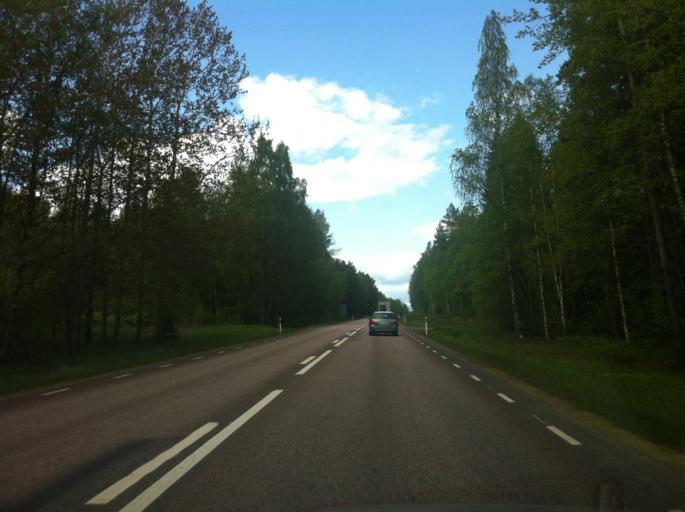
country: SE
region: Vaermland
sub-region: Kristinehamns Kommun
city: Kristinehamn
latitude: 59.3245
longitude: 14.1204
